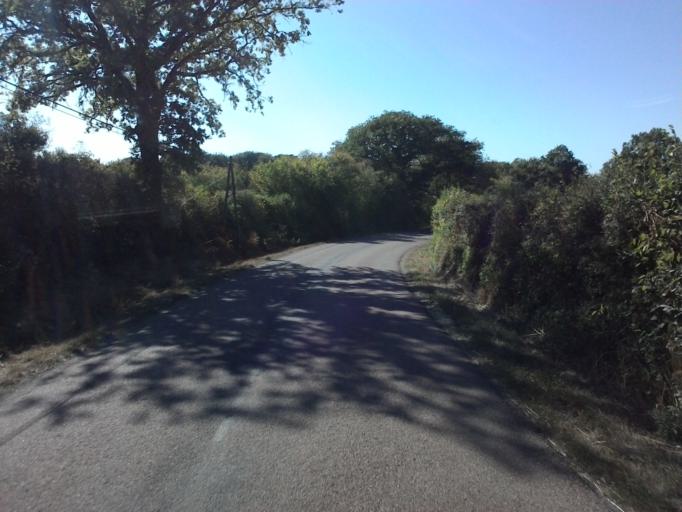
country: FR
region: Bourgogne
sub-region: Departement de la Nievre
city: Lormes
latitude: 47.2690
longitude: 3.9638
